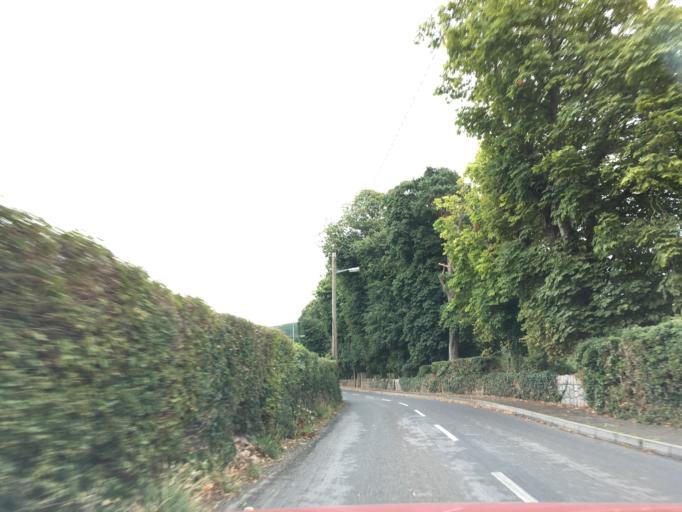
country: IE
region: Munster
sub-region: South Tipperary
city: Cluain Meala
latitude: 52.3657
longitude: -7.5838
